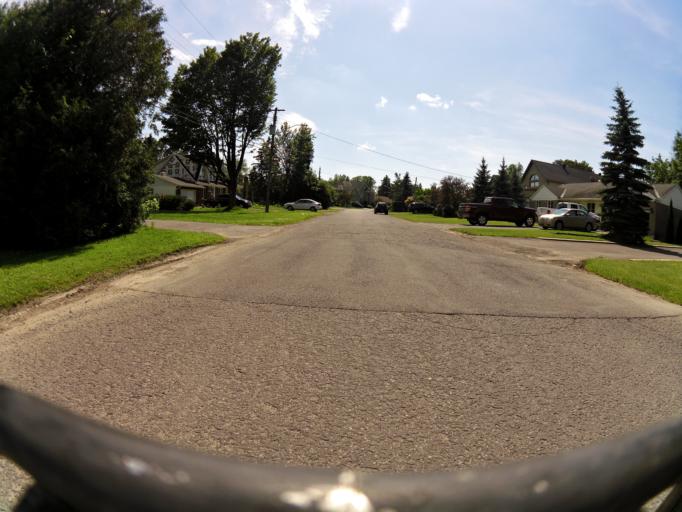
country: CA
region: Ontario
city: Ottawa
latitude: 45.3557
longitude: -75.7157
